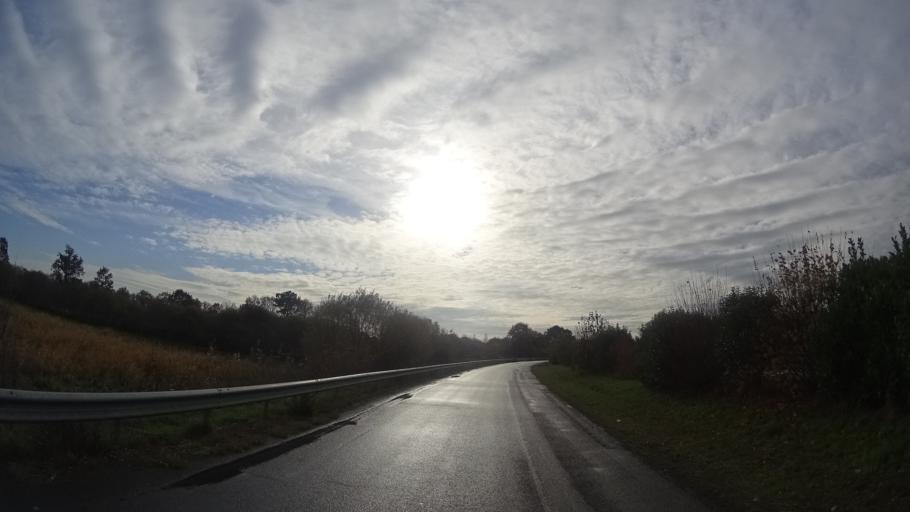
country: FR
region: Brittany
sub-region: Departement du Morbihan
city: Saint-Jean-la-Poterie
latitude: 47.6233
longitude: -2.1016
